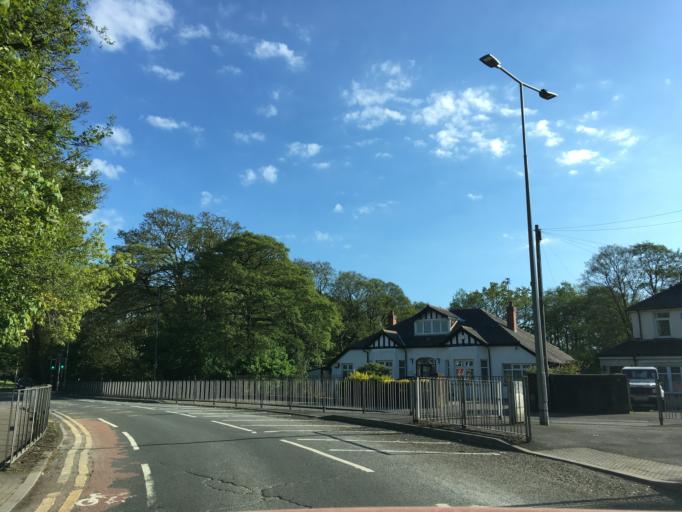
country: GB
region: Wales
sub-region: Cardiff
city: Cardiff
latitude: 51.5178
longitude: -3.1769
